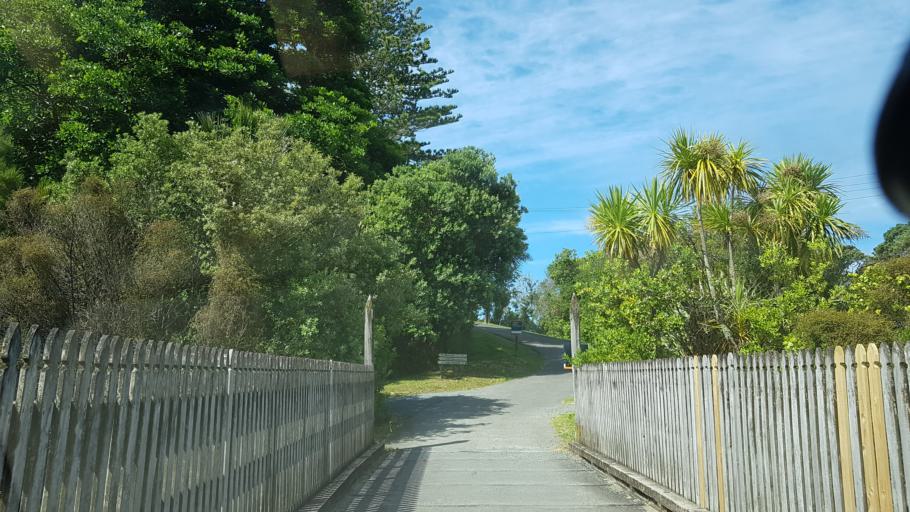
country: NZ
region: Auckland
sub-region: Auckland
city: Rothesay Bay
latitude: -36.6805
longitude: 174.7461
